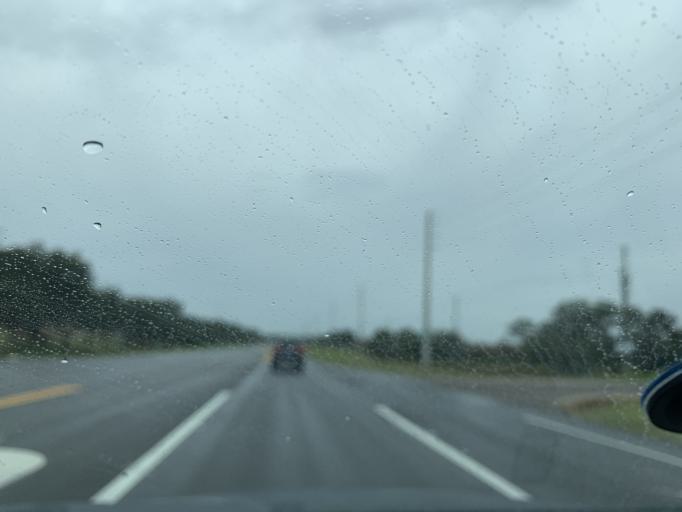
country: US
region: Florida
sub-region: Pasco County
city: Zephyrhills West
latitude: 28.2446
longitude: -82.2204
